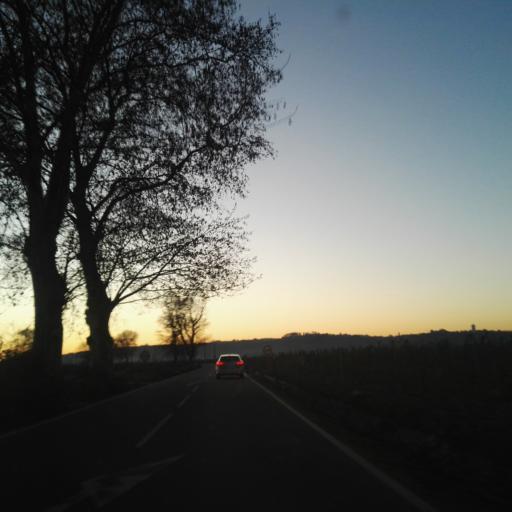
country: PT
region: Santarem
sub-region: Almeirim
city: Almeirim
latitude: 39.2342
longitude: -8.6443
